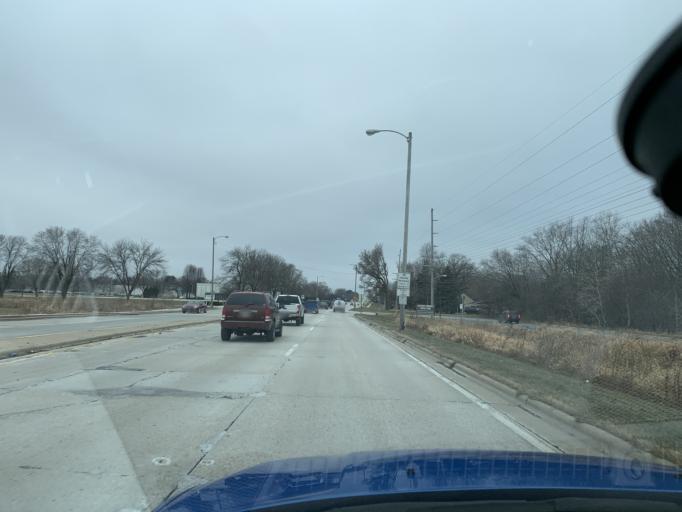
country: US
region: Wisconsin
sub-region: Dane County
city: Sun Prairie
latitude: 43.1876
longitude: -89.2356
